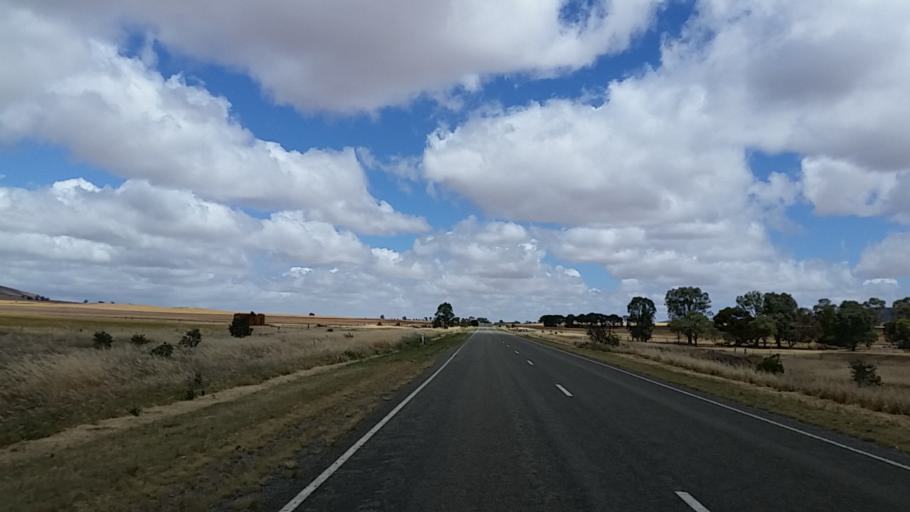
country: AU
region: South Australia
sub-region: Peterborough
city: Peterborough
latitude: -32.8605
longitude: 138.5422
